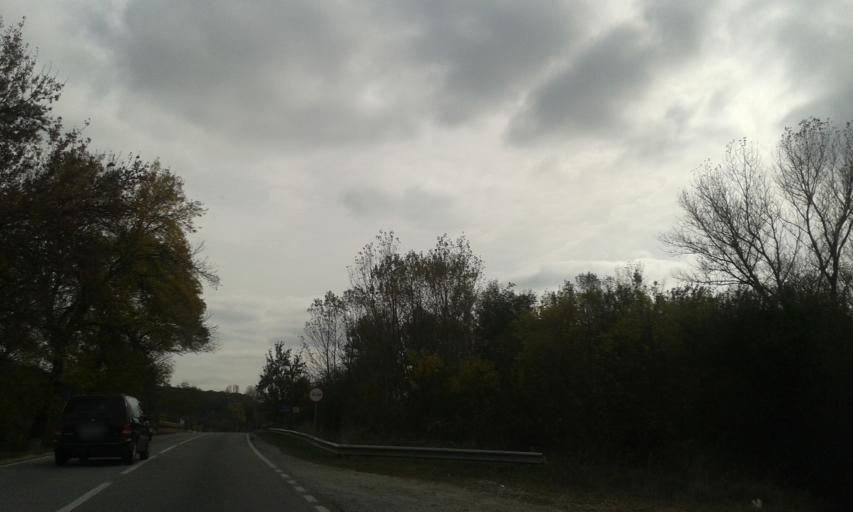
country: RO
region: Gorj
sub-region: Comuna Balanesti
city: Balanesti
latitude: 45.0380
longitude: 23.3704
